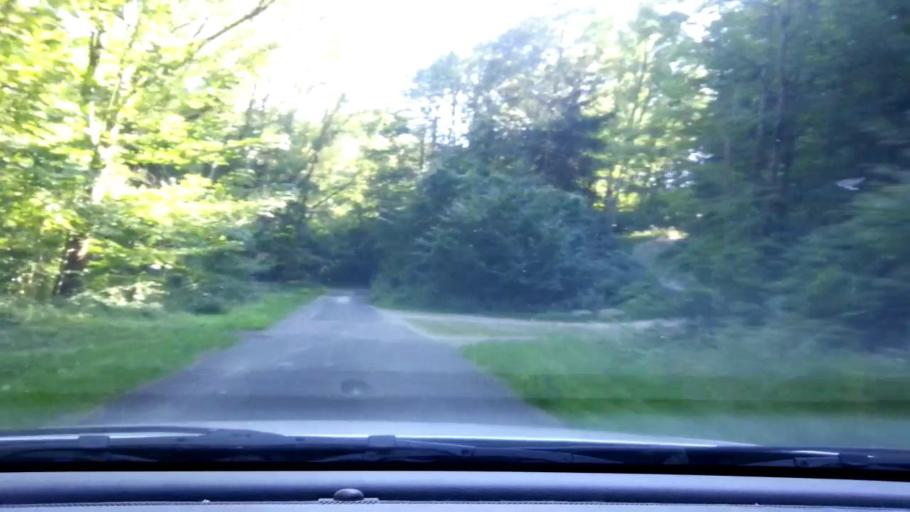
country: DE
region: Bavaria
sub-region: Upper Franconia
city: Wattendorf
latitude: 49.9998
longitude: 11.0924
